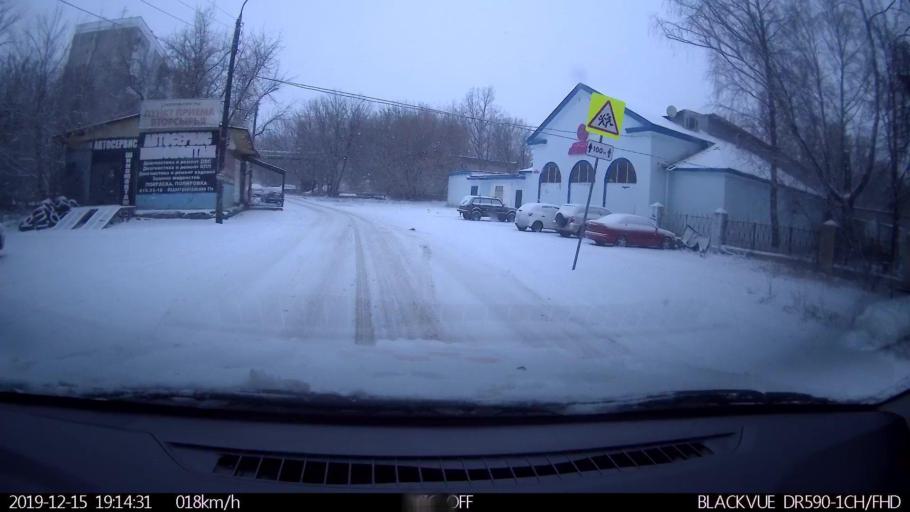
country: RU
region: Nizjnij Novgorod
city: Gorbatovka
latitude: 56.3506
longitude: 43.8445
